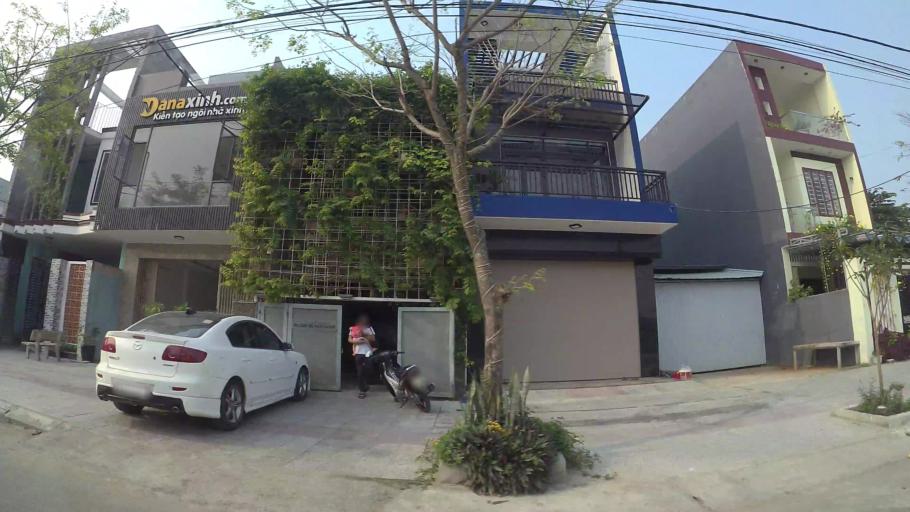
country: VN
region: Da Nang
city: Cam Le
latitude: 16.0068
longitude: 108.2235
